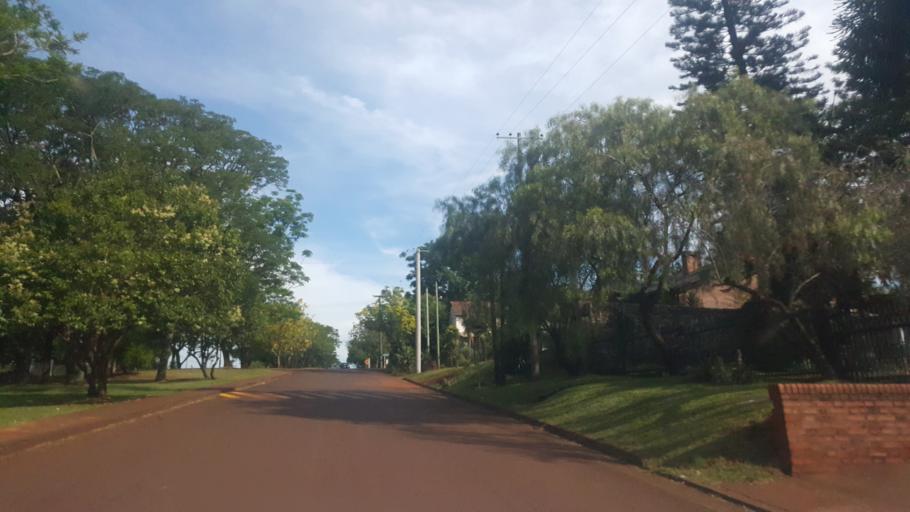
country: AR
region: Misiones
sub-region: Departamento de Leandro N. Alem
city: Leandro N. Alem
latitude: -27.5993
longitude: -55.3311
